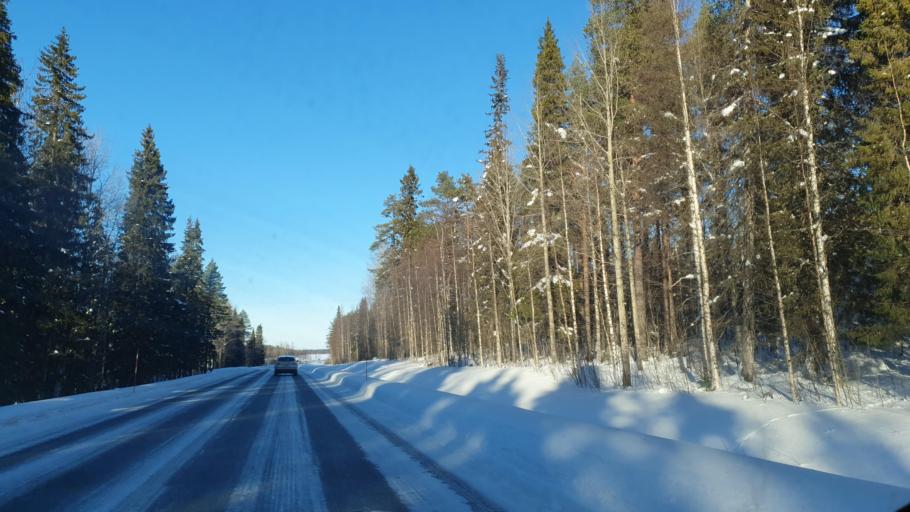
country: FI
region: Lapland
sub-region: Torniolaakso
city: Pello
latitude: 66.6929
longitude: 23.8965
